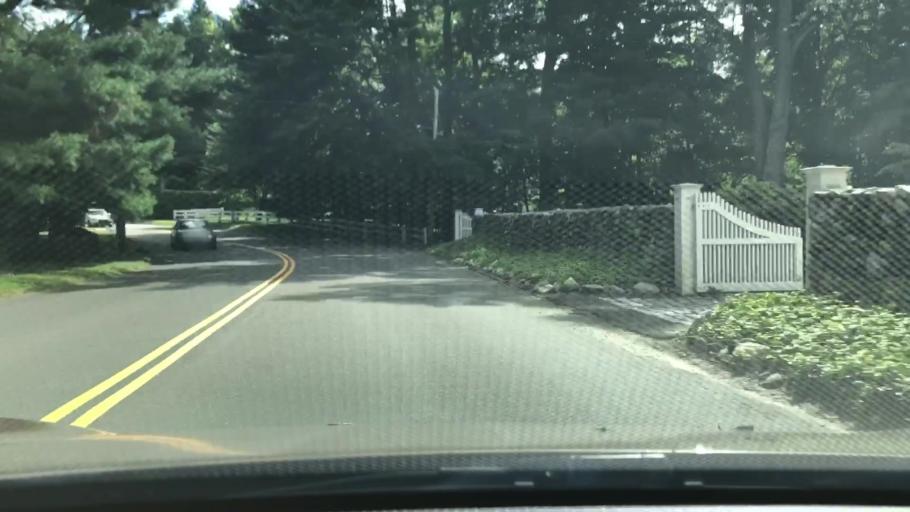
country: US
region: Connecticut
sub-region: Fairfield County
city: Darien
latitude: 41.1134
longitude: -73.4664
